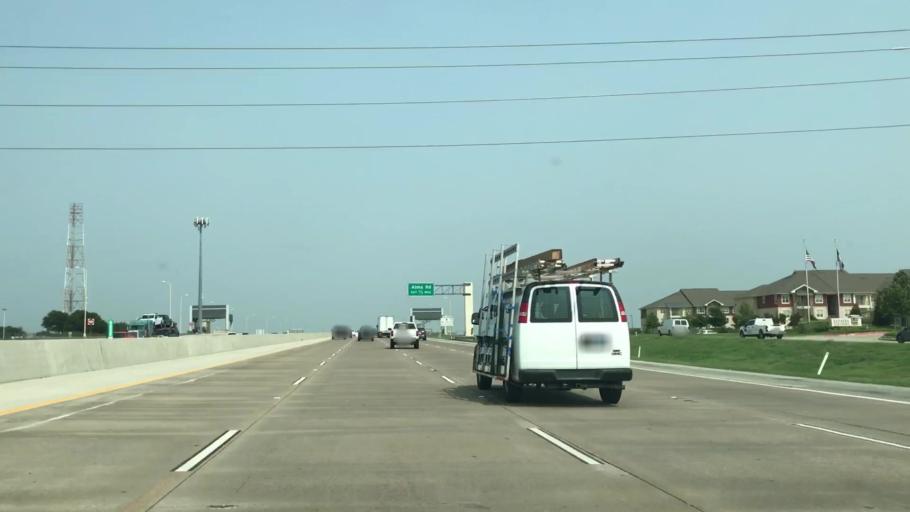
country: US
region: Texas
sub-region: Collin County
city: Plano
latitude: 33.0037
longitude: -96.7406
